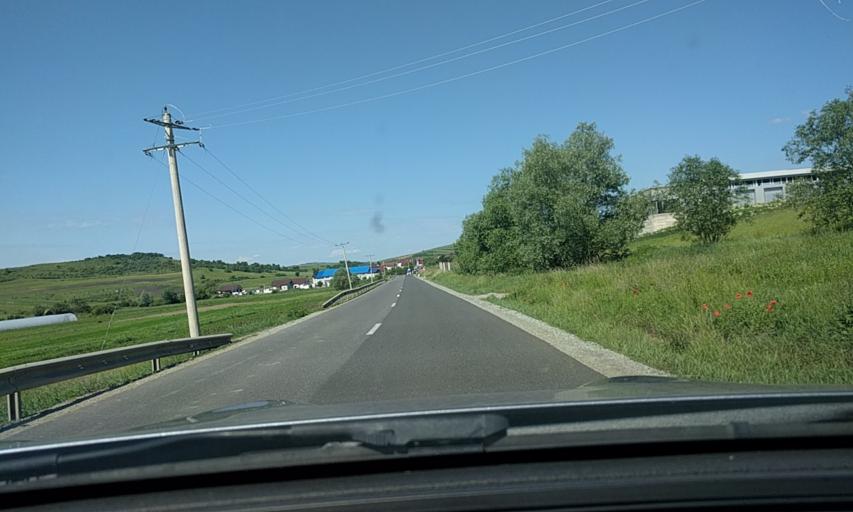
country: RO
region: Bistrita-Nasaud
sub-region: Comuna Dumitra
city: Dumitra
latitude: 47.2321
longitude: 24.4447
